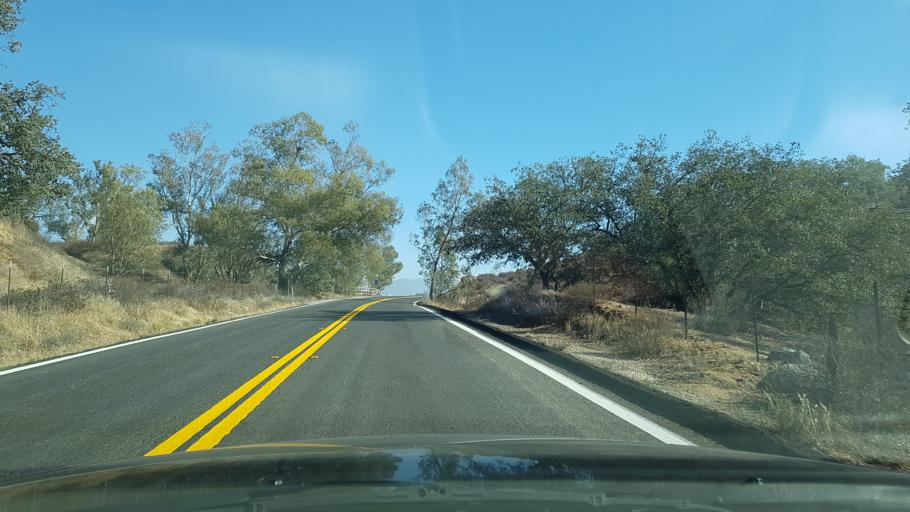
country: US
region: California
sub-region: San Diego County
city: San Diego Country Estates
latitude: 33.0697
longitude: -116.7635
